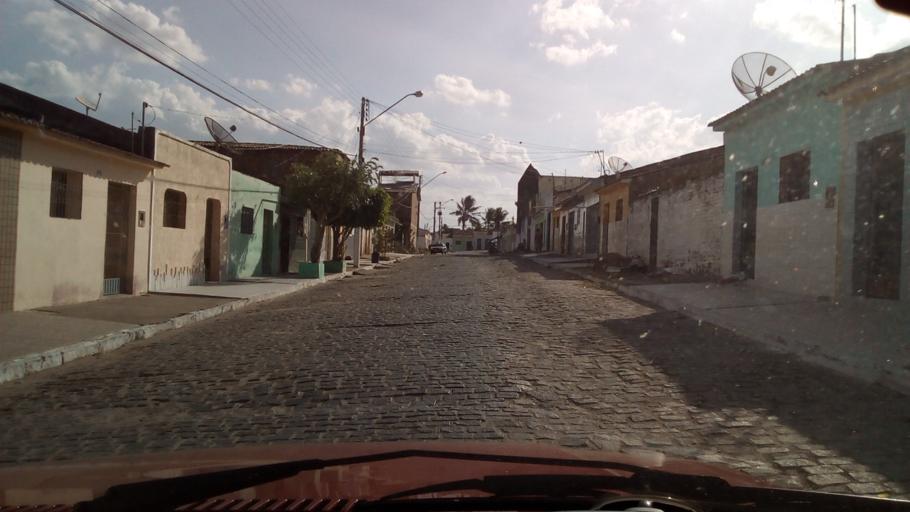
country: BR
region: Paraiba
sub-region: Arara
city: Arara
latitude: -6.8329
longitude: -35.7617
